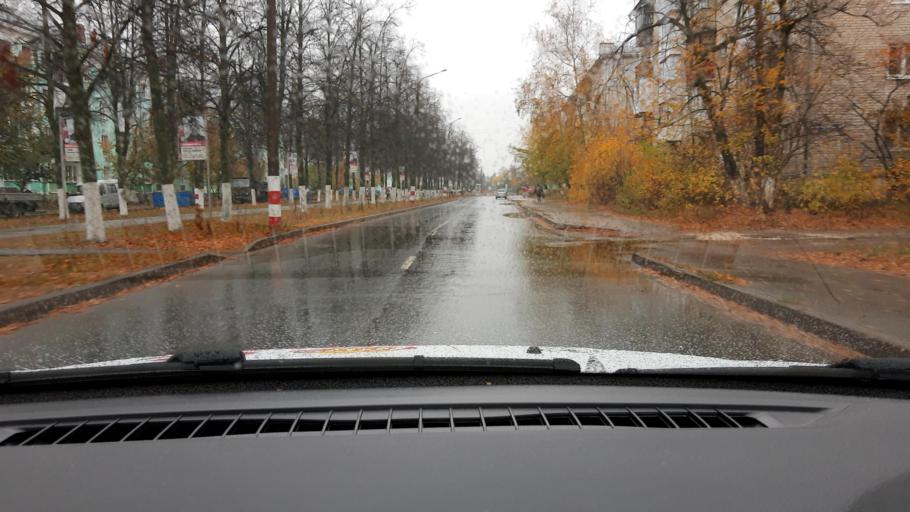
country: RU
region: Nizjnij Novgorod
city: Dzerzhinsk
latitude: 56.2395
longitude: 43.4436
